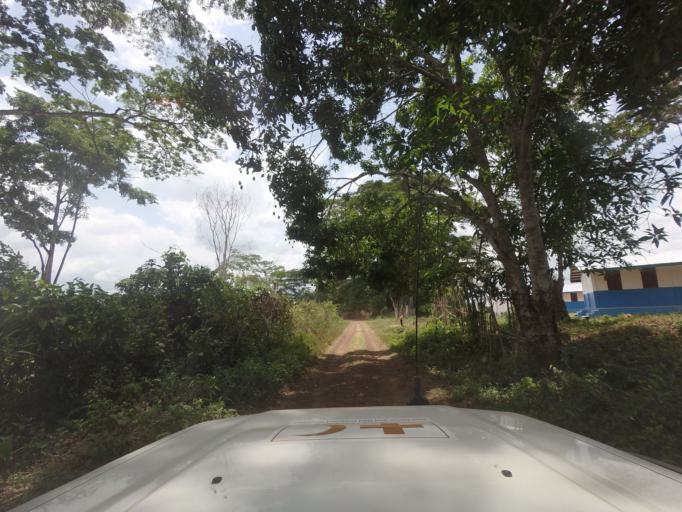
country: LR
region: Bong
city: Gbarnga
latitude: 7.1934
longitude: -9.2045
